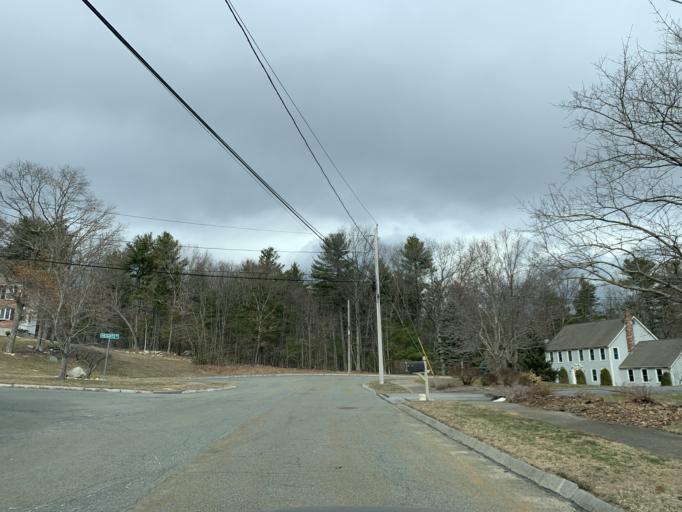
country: US
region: Massachusetts
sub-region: Norfolk County
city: Bellingham
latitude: 42.0464
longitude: -71.4462
